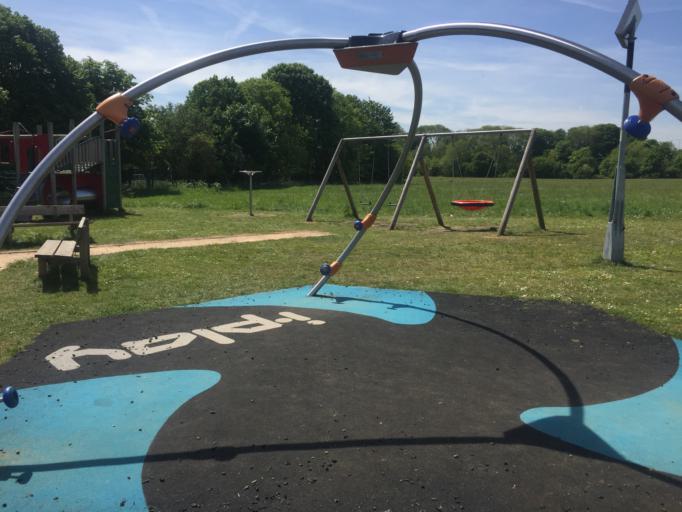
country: GB
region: England
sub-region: Royal Borough of Windsor and Maidenhead
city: Bray
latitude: 51.5072
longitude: -0.6818
